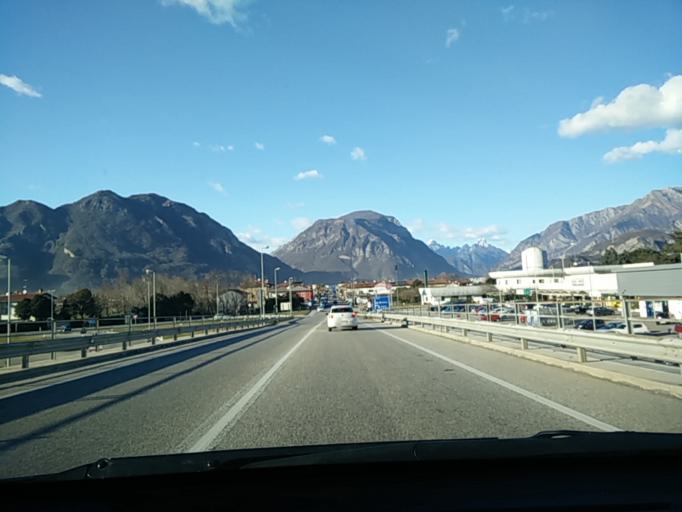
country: IT
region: Friuli Venezia Giulia
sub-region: Provincia di Udine
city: Gemona
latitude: 46.2606
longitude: 13.1084
